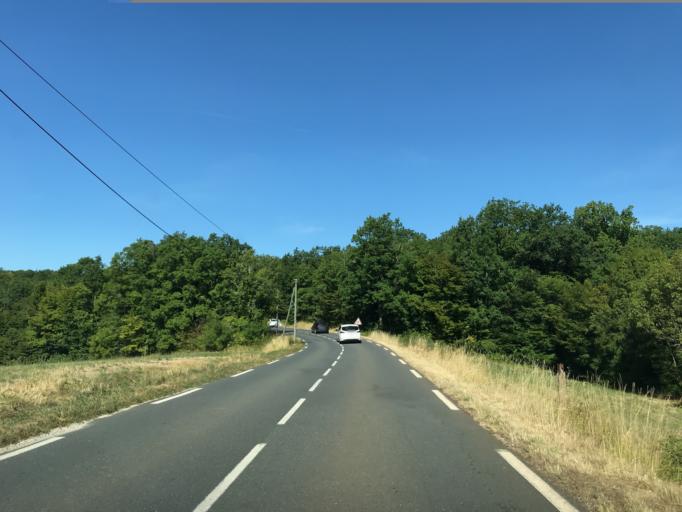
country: FR
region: Limousin
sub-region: Departement de la Correze
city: Larche
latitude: 45.0814
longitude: 1.3767
